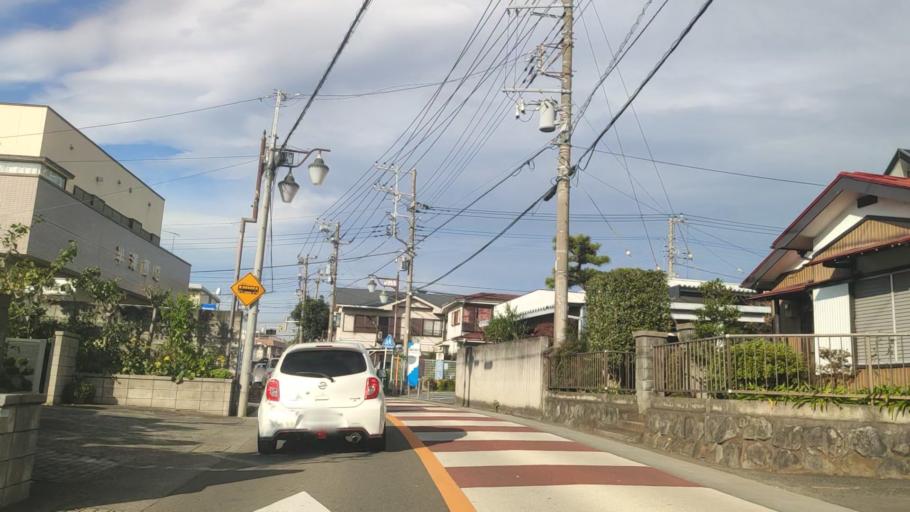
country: JP
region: Kanagawa
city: Zama
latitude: 35.4570
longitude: 139.3988
